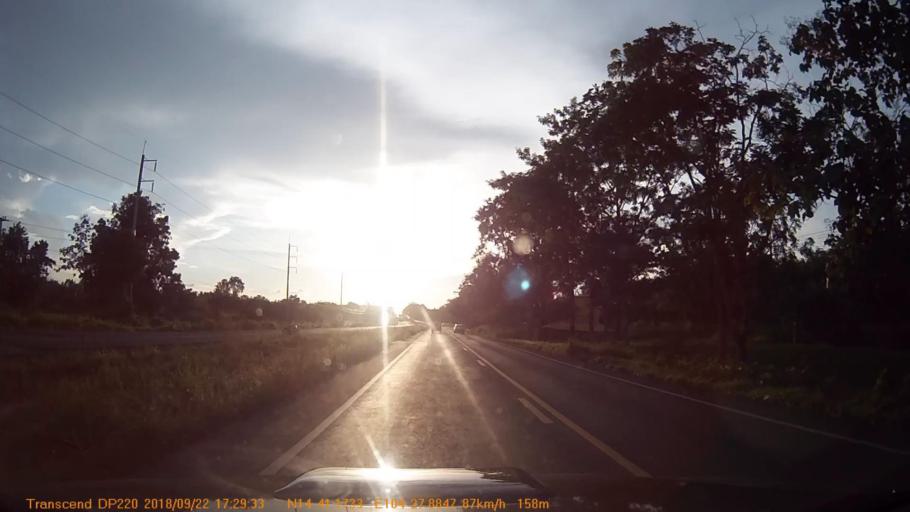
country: TH
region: Sisaket
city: Khun Han
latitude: 14.6862
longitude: 104.4646
